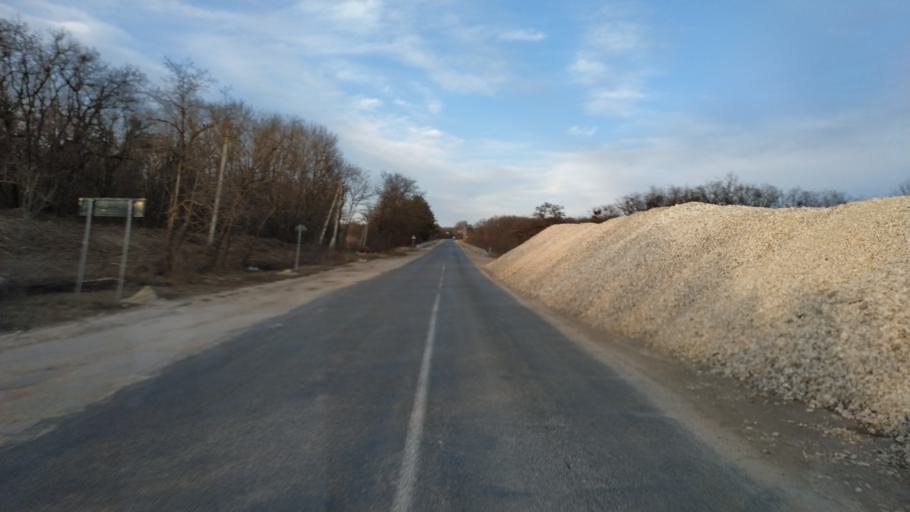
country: MD
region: Nisporeni
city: Nisporeni
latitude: 47.1482
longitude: 28.1500
